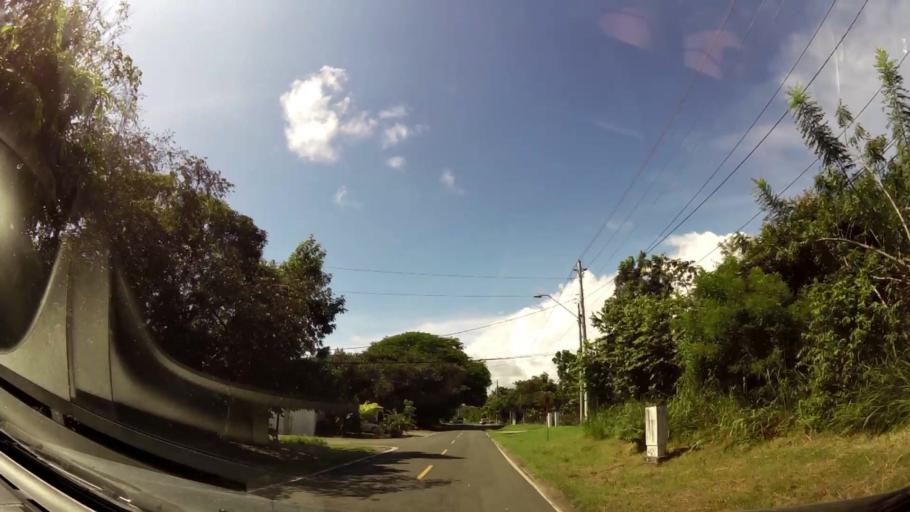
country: PA
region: Panama
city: Nueva Gorgona
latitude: 8.5586
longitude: -79.8779
